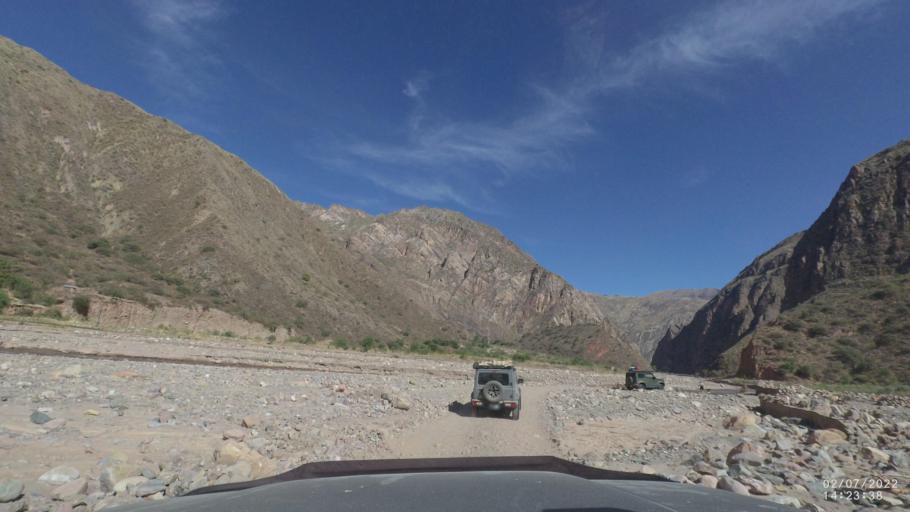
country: BO
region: Cochabamba
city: Irpa Irpa
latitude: -17.8323
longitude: -66.4136
